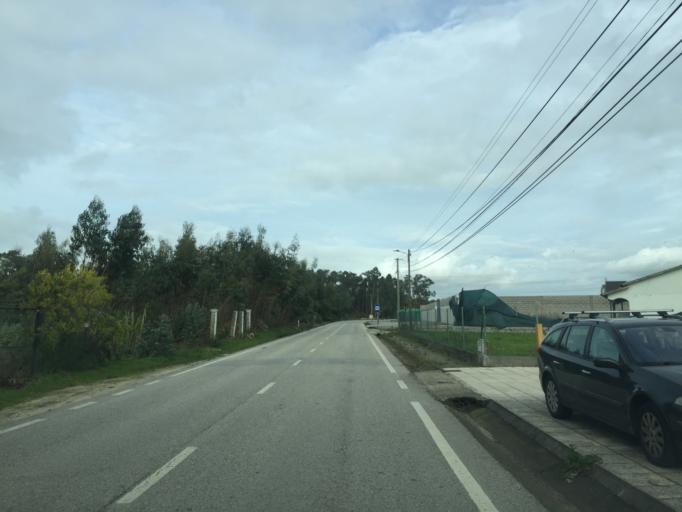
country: PT
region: Coimbra
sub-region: Figueira da Foz
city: Lavos
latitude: 40.0429
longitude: -8.8184
